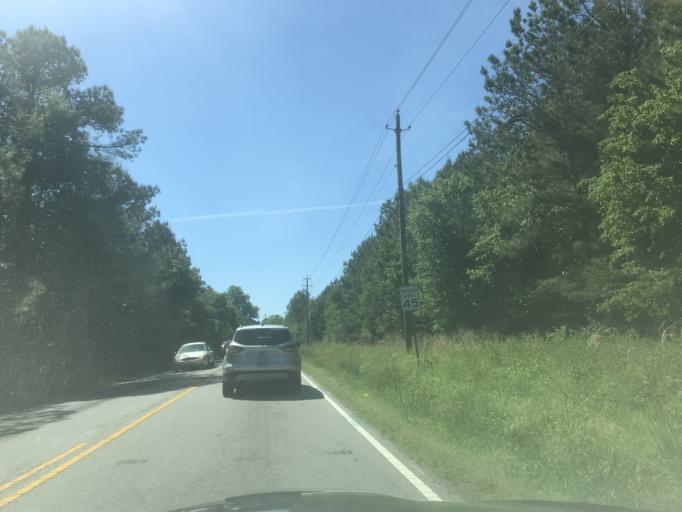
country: US
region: North Carolina
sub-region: Wake County
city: West Raleigh
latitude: 35.7426
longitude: -78.6763
